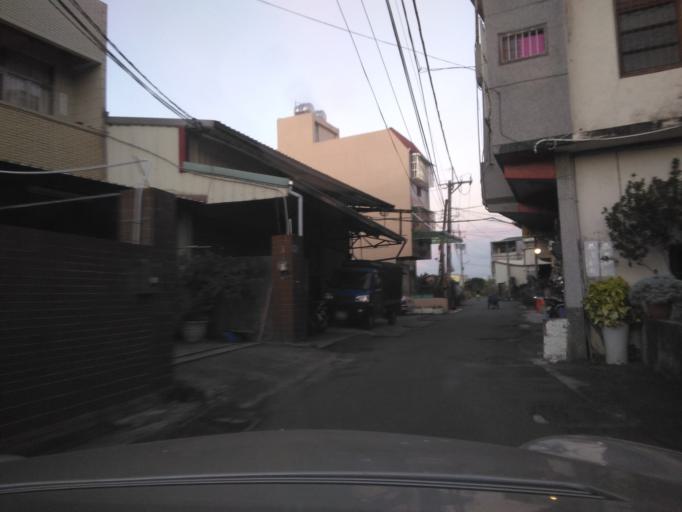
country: TW
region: Taiwan
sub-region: Changhua
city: Chang-hua
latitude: 24.0836
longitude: 120.5875
